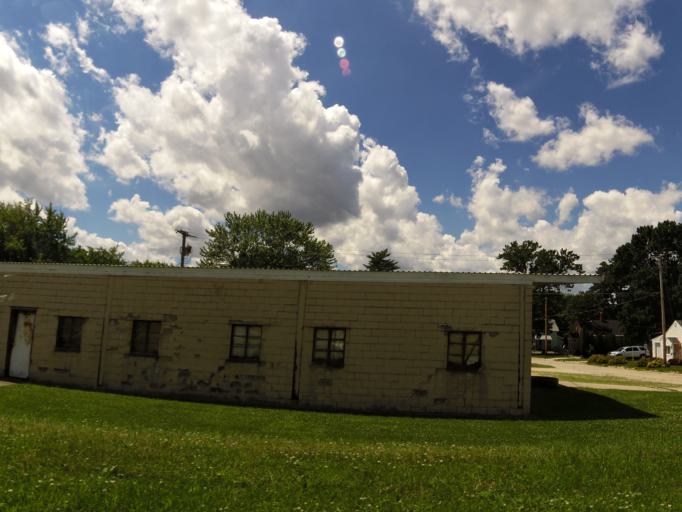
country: US
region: Iowa
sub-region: Fayette County
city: Oelwein
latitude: 42.6705
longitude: -91.9110
